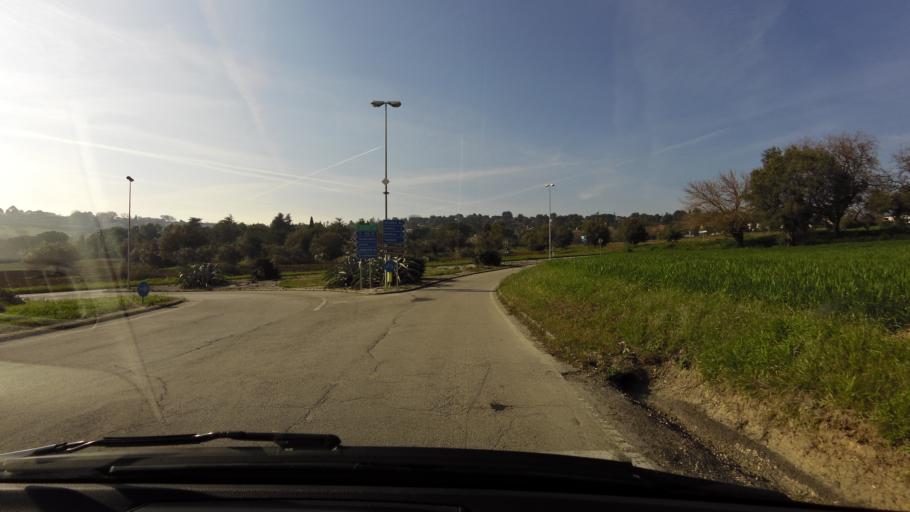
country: IT
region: The Marches
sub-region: Provincia di Ancona
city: Marcelli
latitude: 43.4999
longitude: 13.6172
